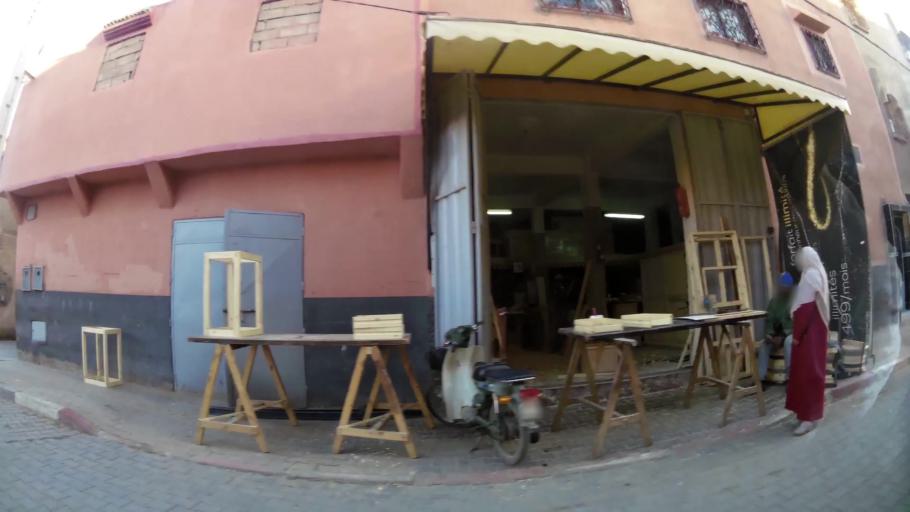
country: MA
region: Marrakech-Tensift-Al Haouz
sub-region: Kelaa-Des-Sraghna
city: Sidi Abdallah
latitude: 32.2453
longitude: -7.9515
